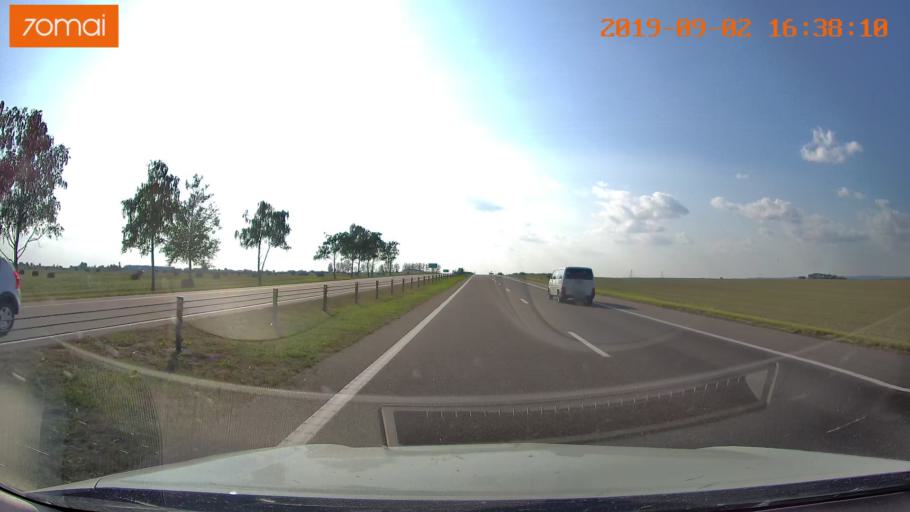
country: BY
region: Minsk
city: Zamostochcha
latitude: 53.7615
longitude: 27.9249
